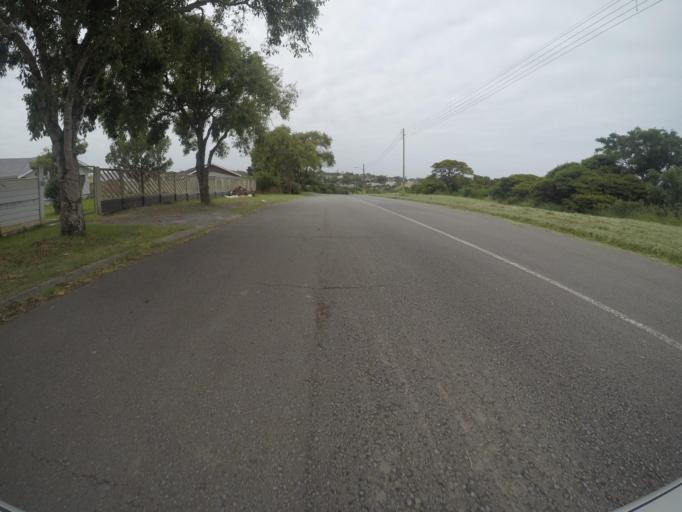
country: ZA
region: Eastern Cape
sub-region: Buffalo City Metropolitan Municipality
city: East London
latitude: -32.9755
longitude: 27.9440
